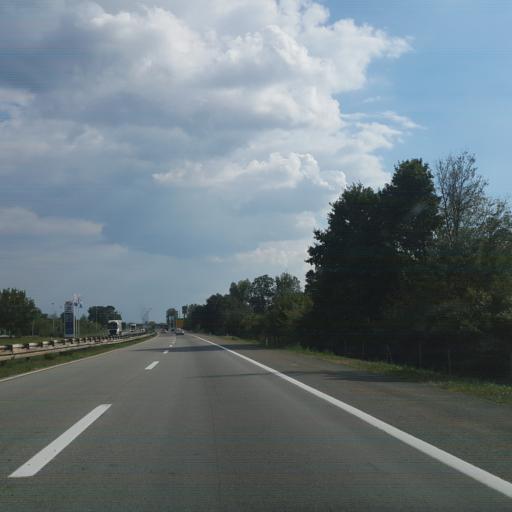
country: RS
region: Central Serbia
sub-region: Podunavski Okrug
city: Velika Plana
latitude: 44.3502
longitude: 21.0750
